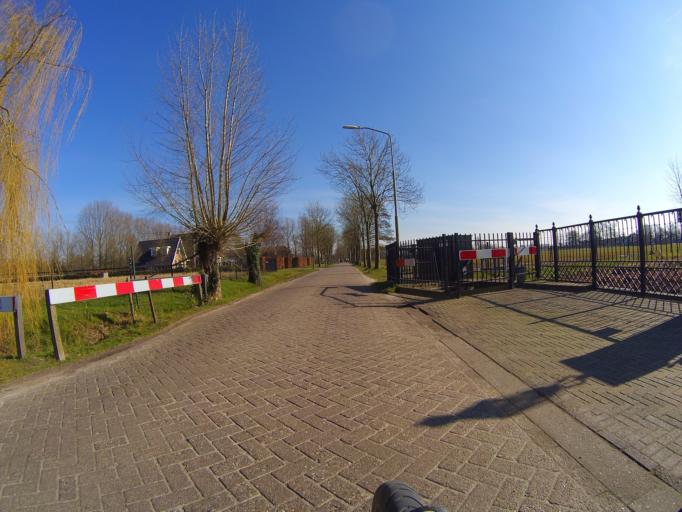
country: NL
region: Gelderland
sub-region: Gemeente Nijkerk
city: Nijkerk
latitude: 52.2114
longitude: 5.4832
